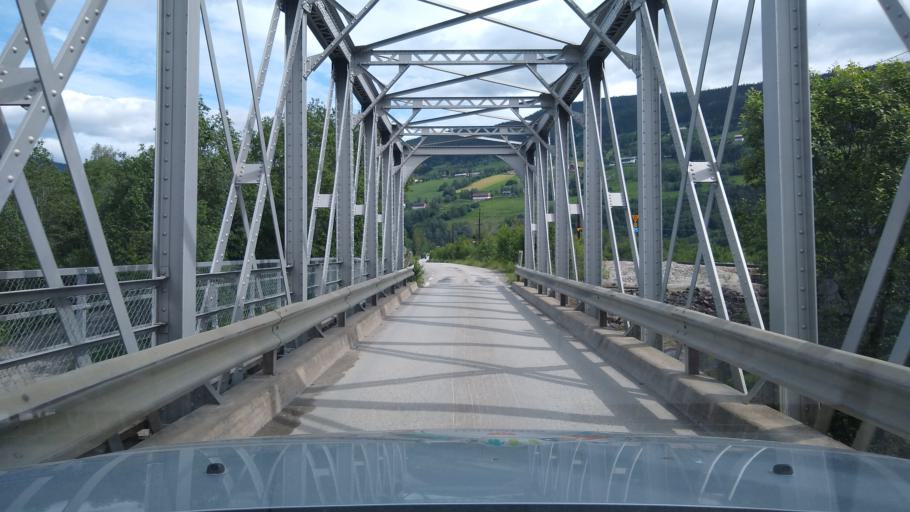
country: NO
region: Oppland
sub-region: Ringebu
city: Ringebu
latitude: 61.5195
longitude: 10.1425
